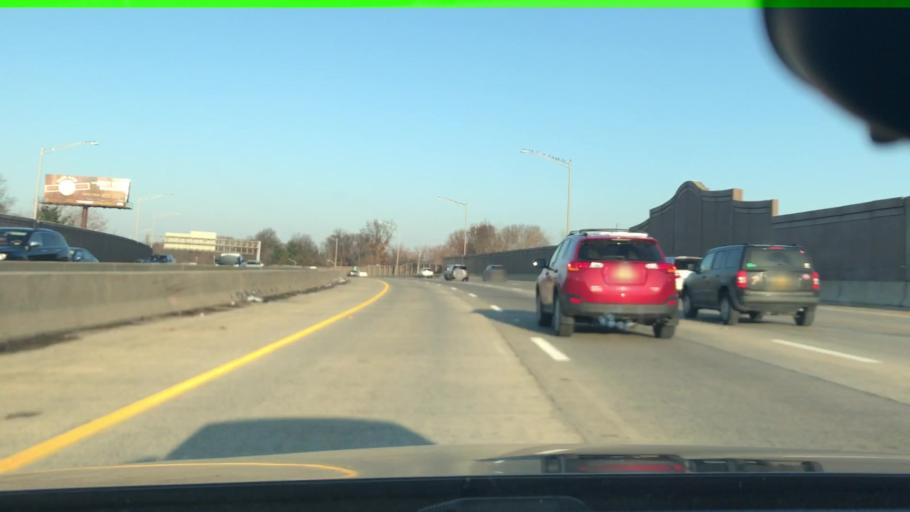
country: US
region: New Jersey
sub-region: Bergen County
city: Rochelle Park
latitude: 40.8995
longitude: -74.0815
